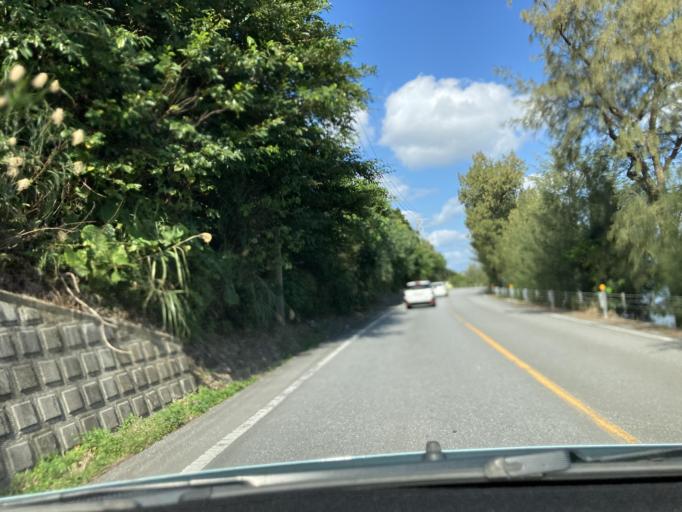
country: JP
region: Okinawa
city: Nago
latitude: 26.6390
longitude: 128.0024
